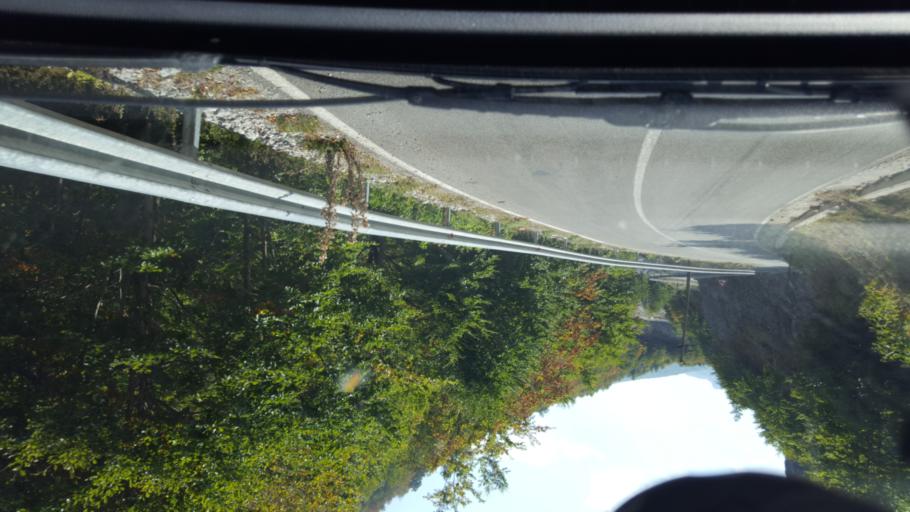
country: ME
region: Andrijevica
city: Andrijevica
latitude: 42.5639
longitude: 19.7339
